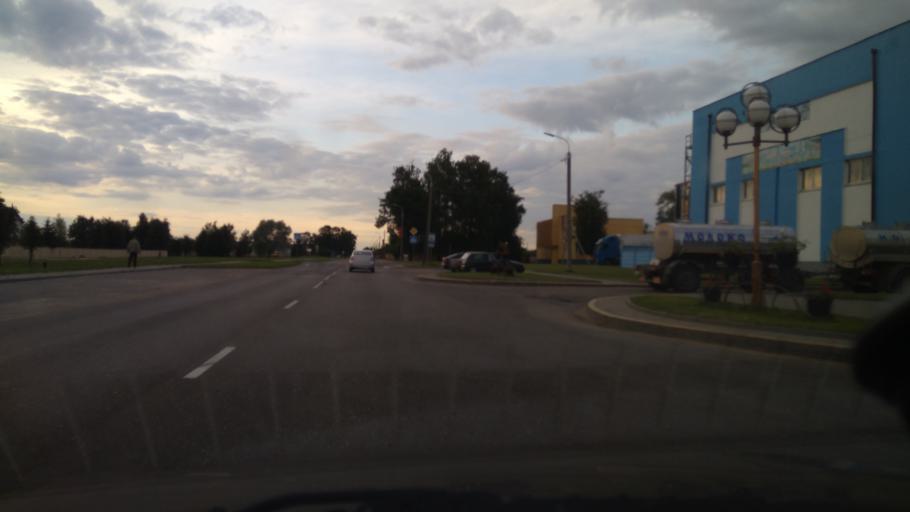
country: BY
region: Grodnenskaya
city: Shchuchin
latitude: 53.5931
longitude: 24.7447
